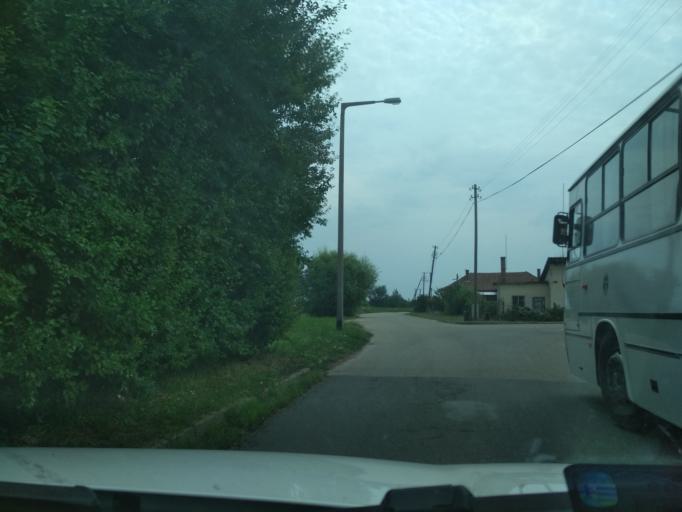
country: HU
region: Jasz-Nagykun-Szolnok
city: Tiszafured
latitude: 47.6276
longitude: 20.7571
